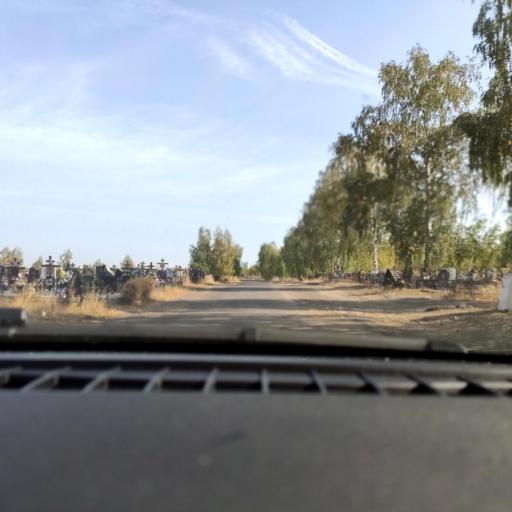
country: RU
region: Voronezj
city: Maslovka
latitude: 51.5122
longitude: 39.2013
